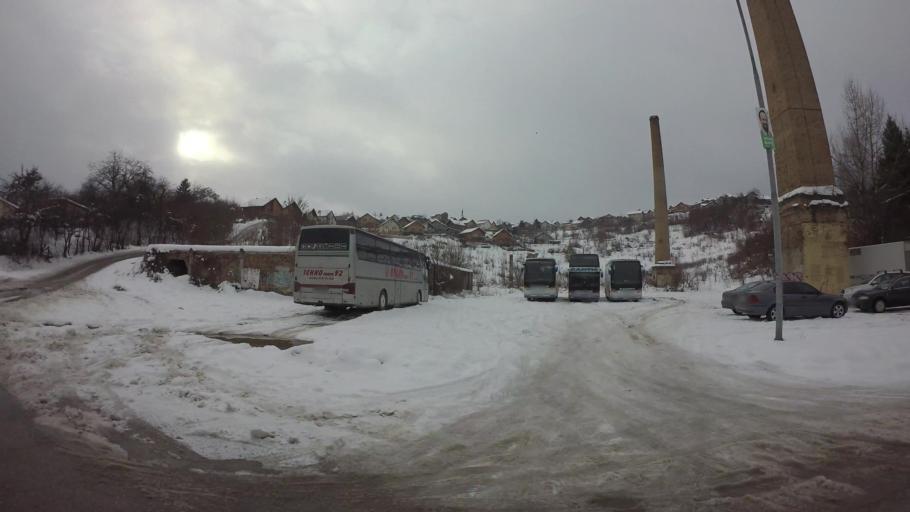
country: BA
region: Federation of Bosnia and Herzegovina
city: Kobilja Glava
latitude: 43.8627
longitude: 18.3998
